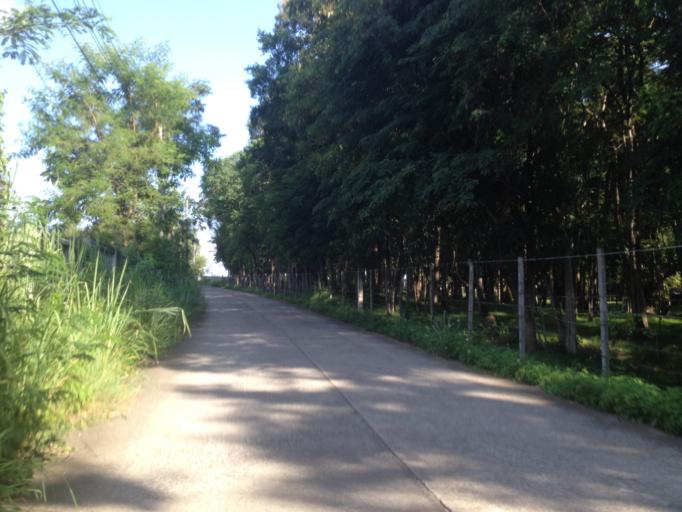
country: TH
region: Chiang Mai
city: Chiang Mai
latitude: 18.7555
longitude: 98.9325
